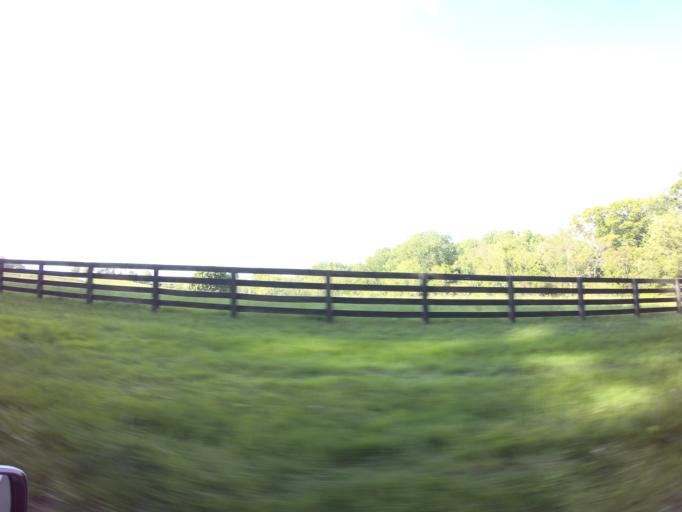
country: US
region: Maryland
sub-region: Baltimore County
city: Hunt Valley
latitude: 39.5049
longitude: -76.6980
